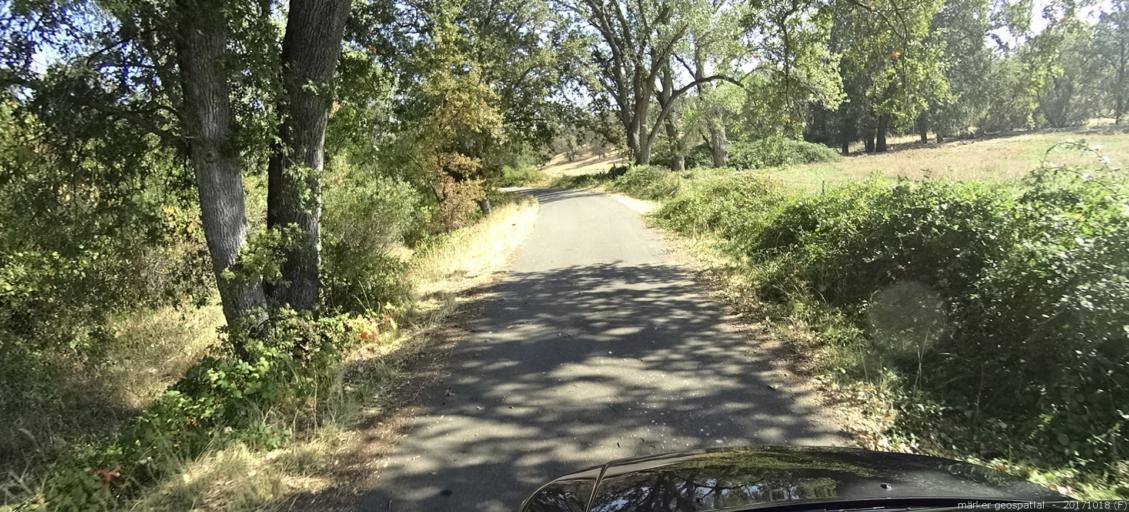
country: US
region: California
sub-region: Shasta County
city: Shingletown
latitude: 40.5644
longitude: -122.0315
